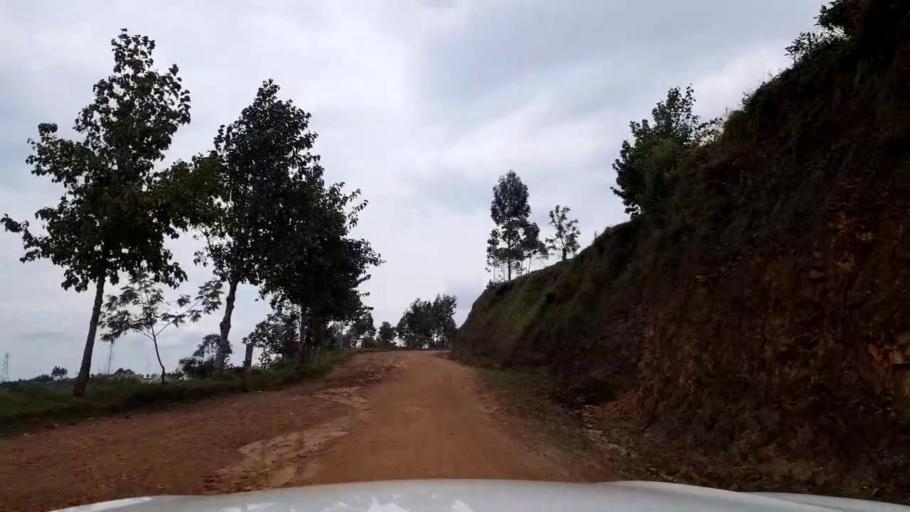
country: RW
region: Western Province
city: Kibuye
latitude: -1.9595
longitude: 29.4046
